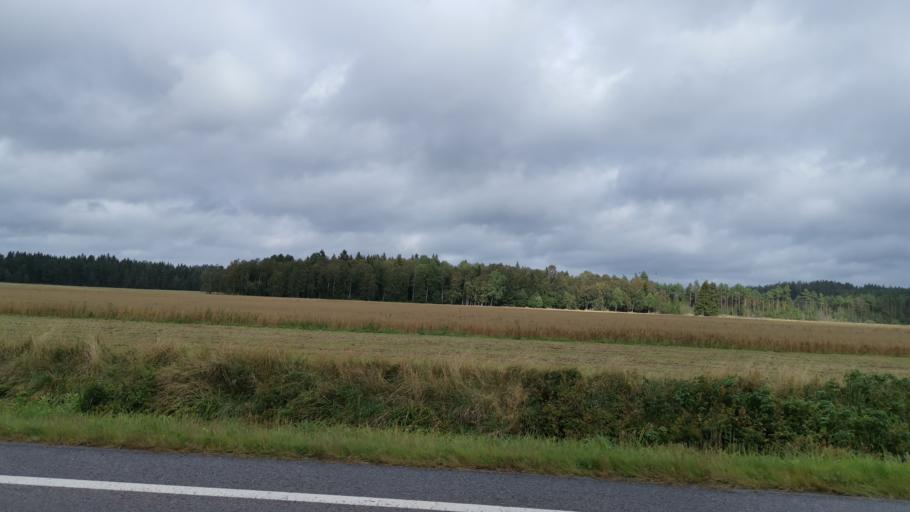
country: SE
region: Vaestra Goetaland
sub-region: Uddevalla Kommun
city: Uddevalla
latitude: 58.3439
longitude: 12.0478
